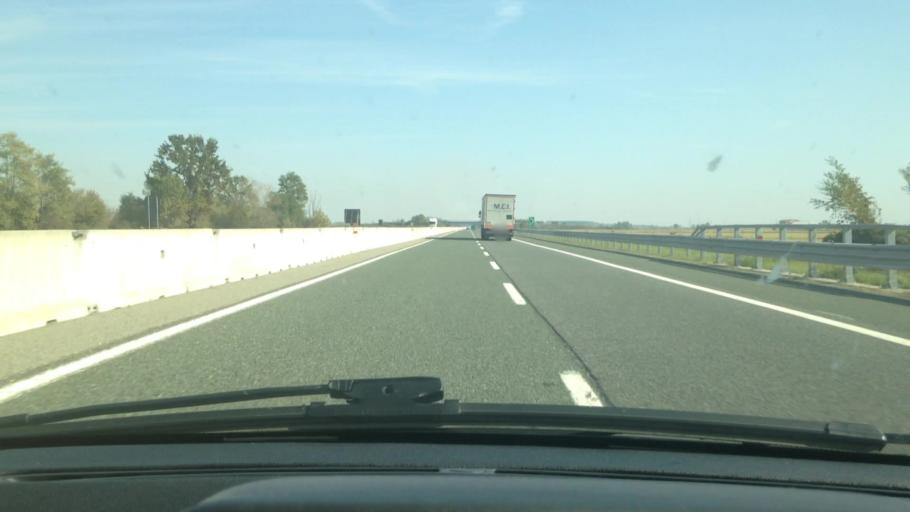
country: IT
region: Piedmont
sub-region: Provincia di Vercelli
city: Sali Vercellese
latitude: 45.3047
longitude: 8.3090
